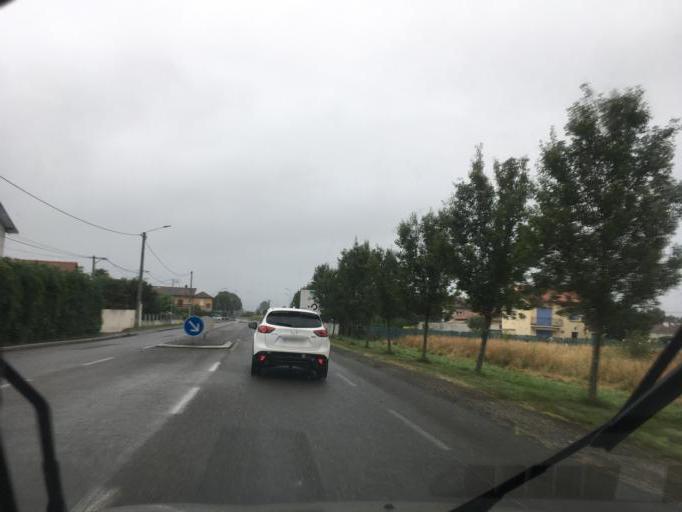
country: FR
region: Midi-Pyrenees
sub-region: Departement des Hautes-Pyrenees
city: Bazet
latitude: 43.2882
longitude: 0.0692
